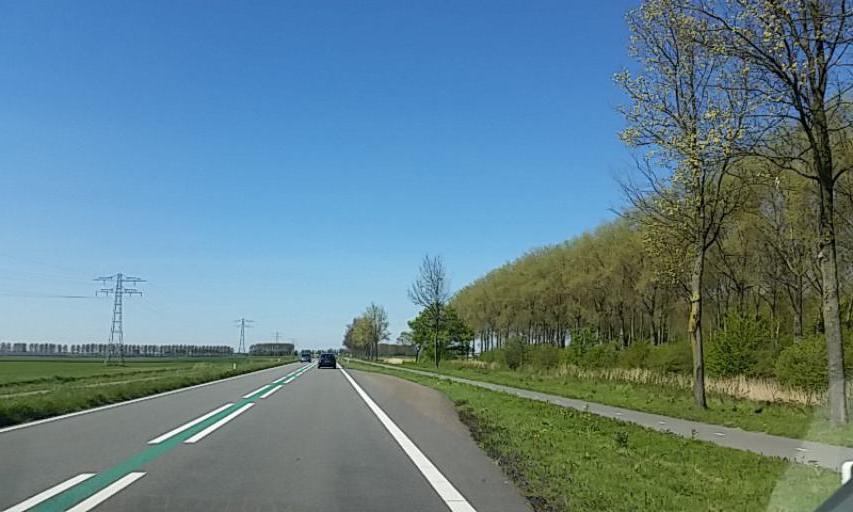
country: NL
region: Zeeland
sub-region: Gemeente Terneuzen
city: Axel
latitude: 51.2497
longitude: 3.8870
